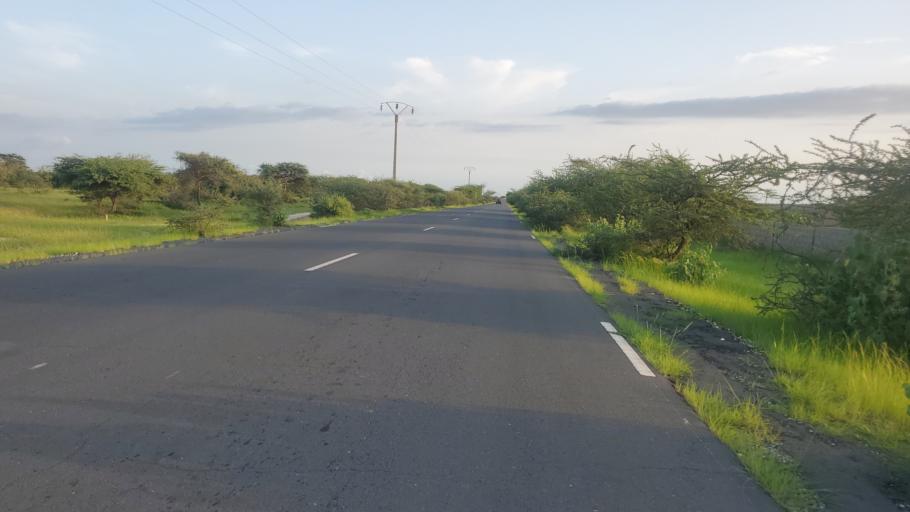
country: SN
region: Saint-Louis
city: Saint-Louis
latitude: 16.1751
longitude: -16.4097
